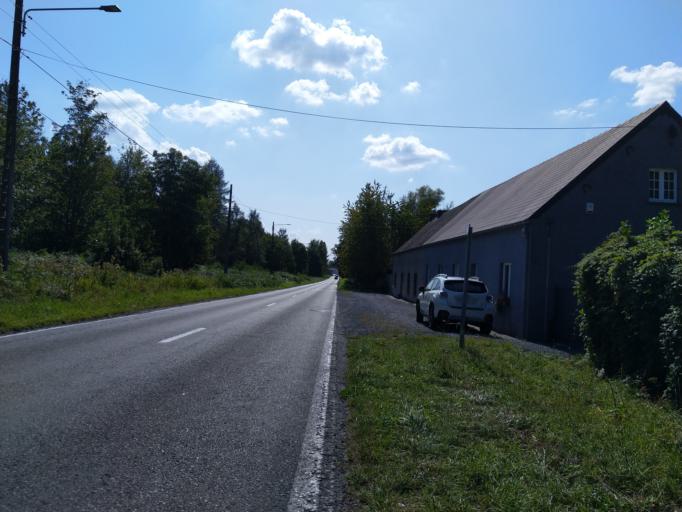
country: BE
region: Wallonia
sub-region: Province du Hainaut
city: Saint-Ghislain
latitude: 50.4994
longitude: 3.8323
